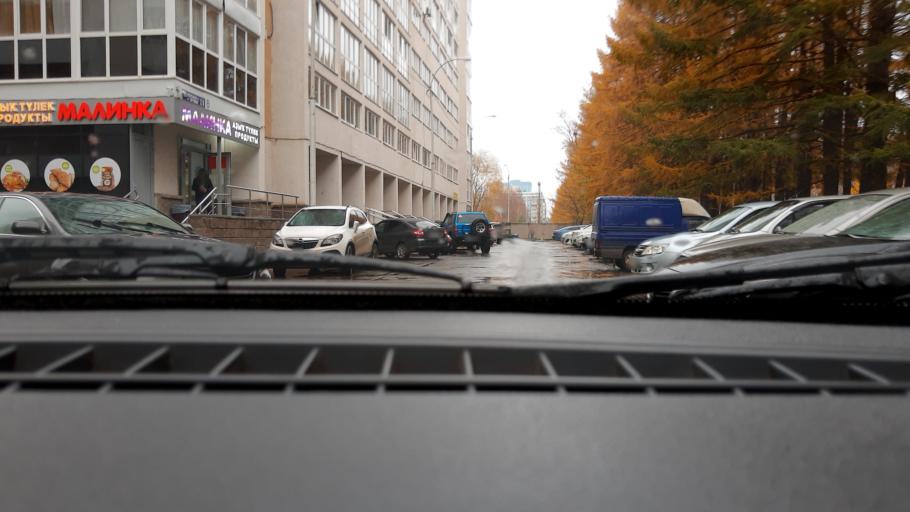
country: RU
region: Bashkortostan
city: Mikhaylovka
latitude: 54.7920
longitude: 55.8545
